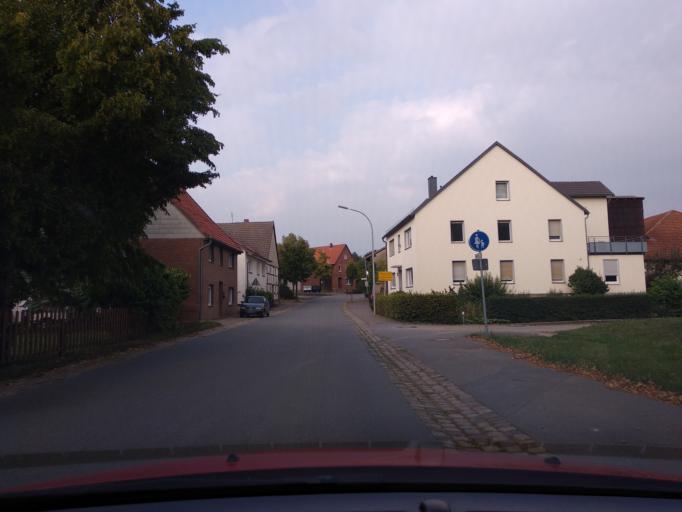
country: DE
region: Hesse
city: Liebenau
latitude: 51.5348
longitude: 9.2760
